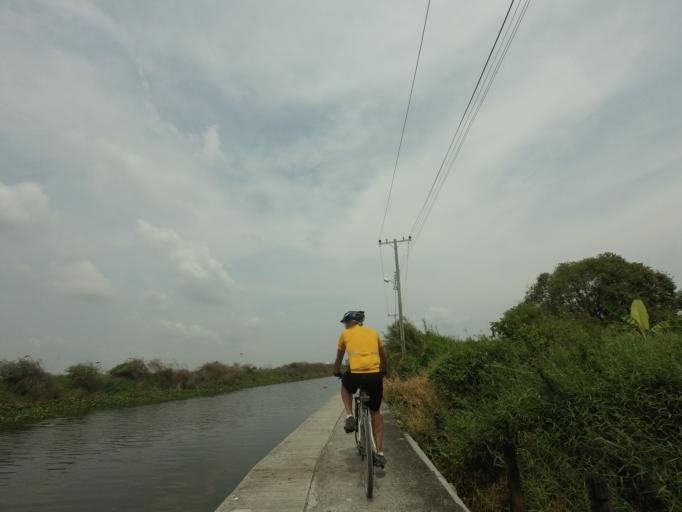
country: TH
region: Bangkok
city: Lat Krabang
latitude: 13.7009
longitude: 100.7786
